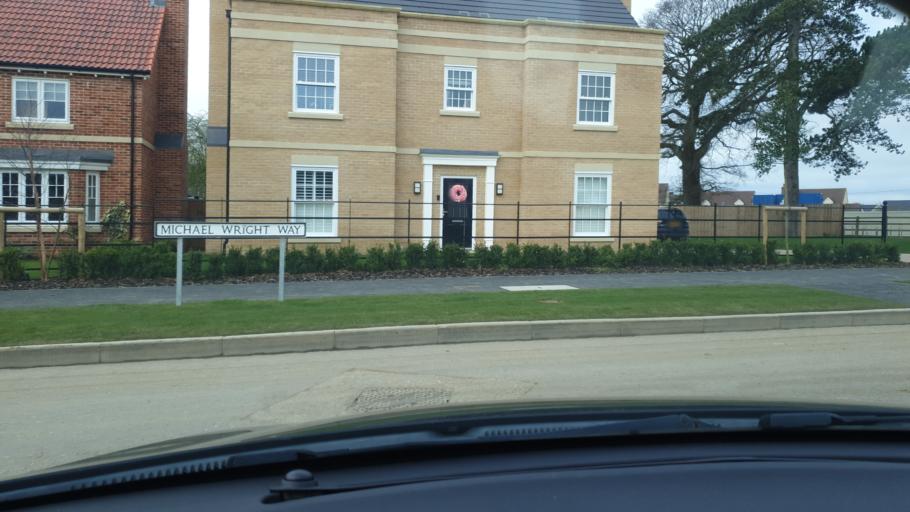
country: GB
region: England
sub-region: Essex
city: Great Bentley
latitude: 51.8583
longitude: 1.0663
